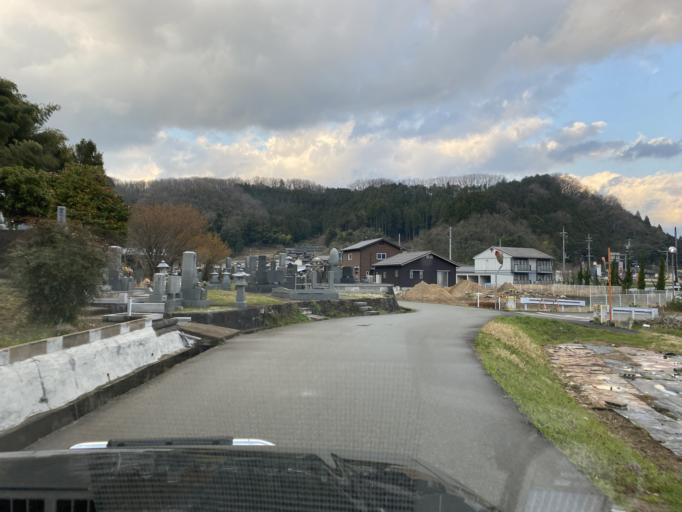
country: JP
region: Hyogo
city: Toyooka
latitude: 35.4706
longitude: 134.7680
